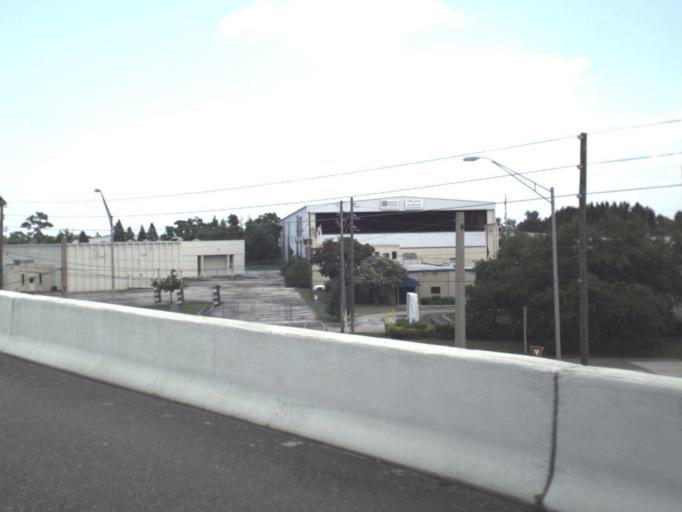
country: US
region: Florida
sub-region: Pinellas County
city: South Highpoint
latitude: 27.8859
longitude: -82.7167
